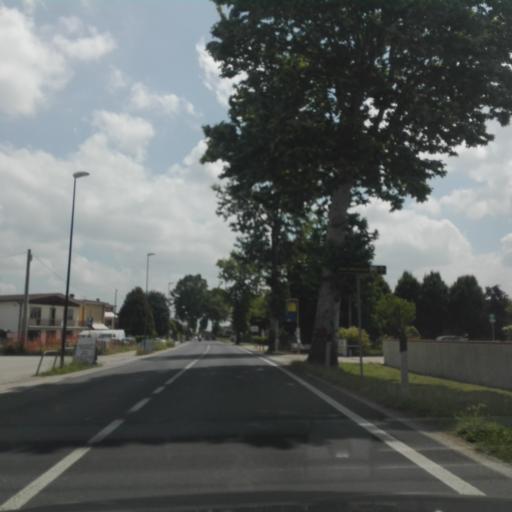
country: IT
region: Veneto
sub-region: Provincia di Rovigo
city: Villadose
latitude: 45.0658
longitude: 11.8994
